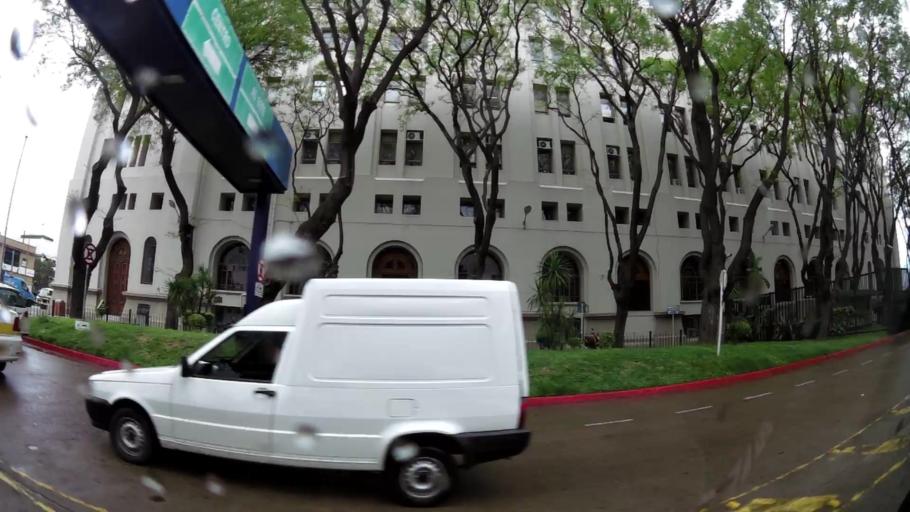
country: UY
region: Montevideo
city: Montevideo
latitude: -34.9045
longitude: -56.2114
